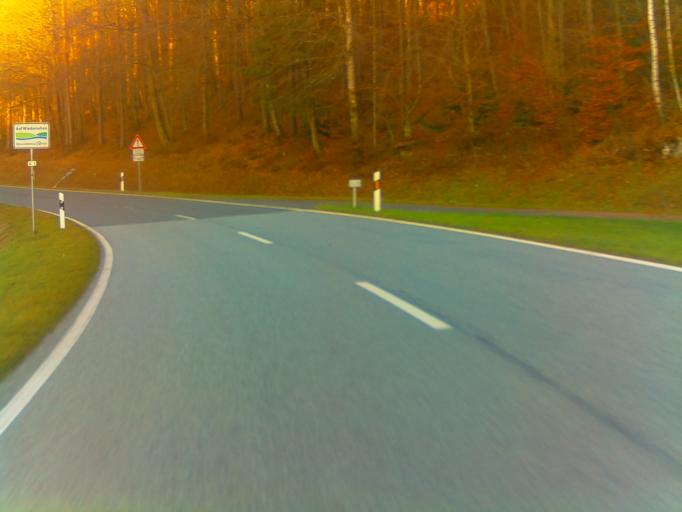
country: DE
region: Bavaria
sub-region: Regierungsbezirk Unterfranken
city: Kirchzell
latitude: 49.5785
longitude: 9.1483
